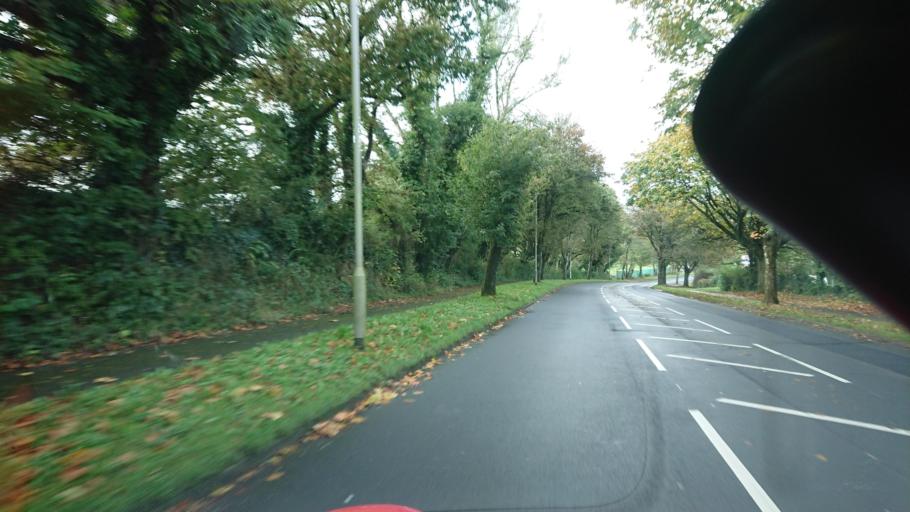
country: GB
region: England
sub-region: Cornwall
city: Torpoint
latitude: 50.4135
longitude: -4.1831
